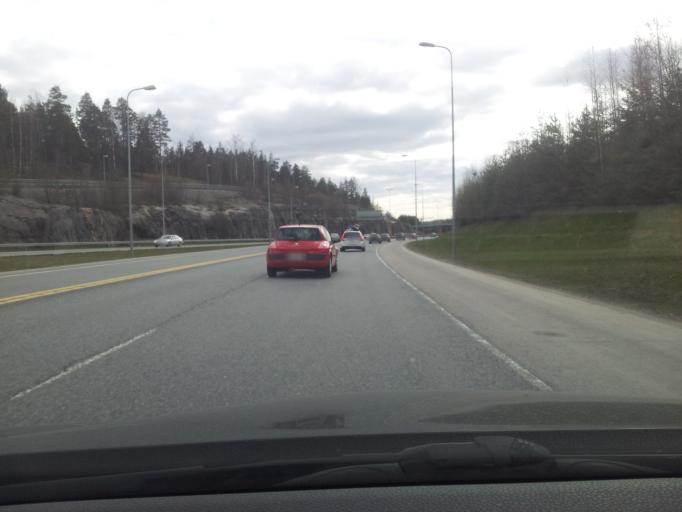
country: FI
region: Uusimaa
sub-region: Helsinki
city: Kauniainen
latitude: 60.2007
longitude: 24.7469
